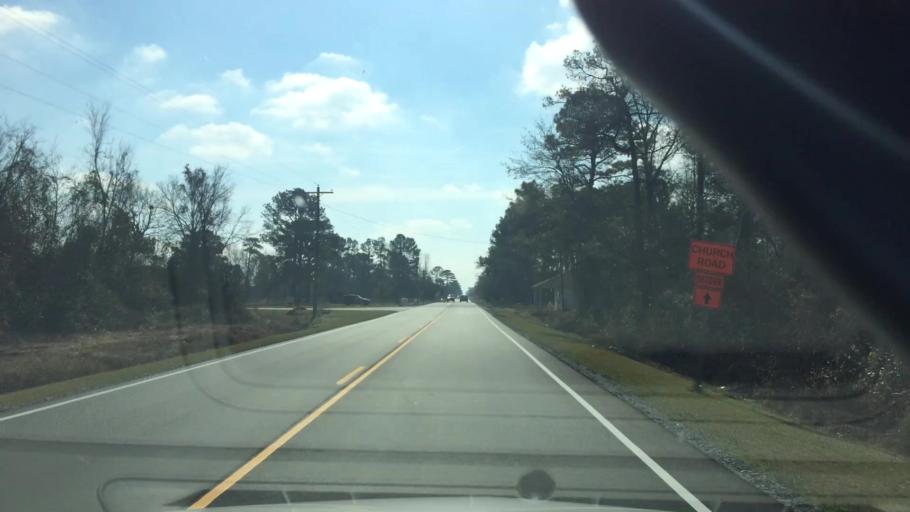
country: US
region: North Carolina
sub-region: Duplin County
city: Beulaville
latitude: 35.0030
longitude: -77.7546
